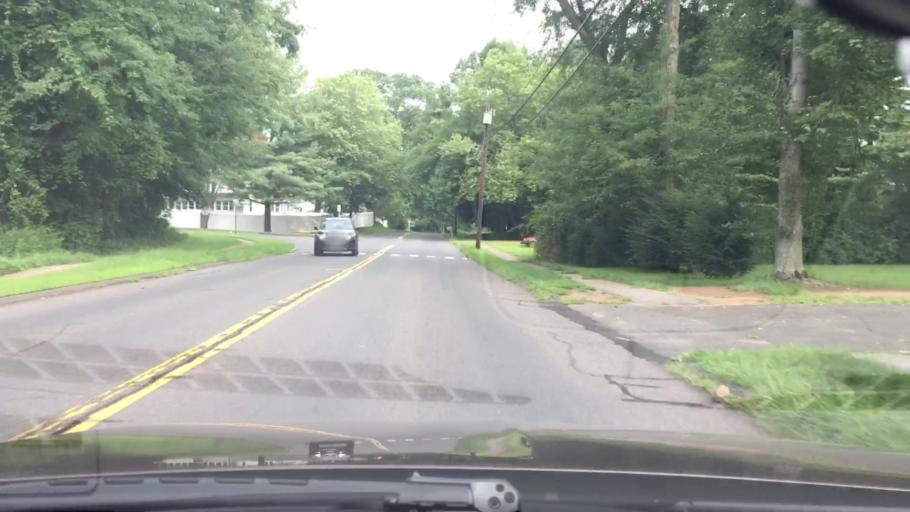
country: US
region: Connecticut
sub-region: Tolland County
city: Rockville
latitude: 41.8303
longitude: -72.4912
